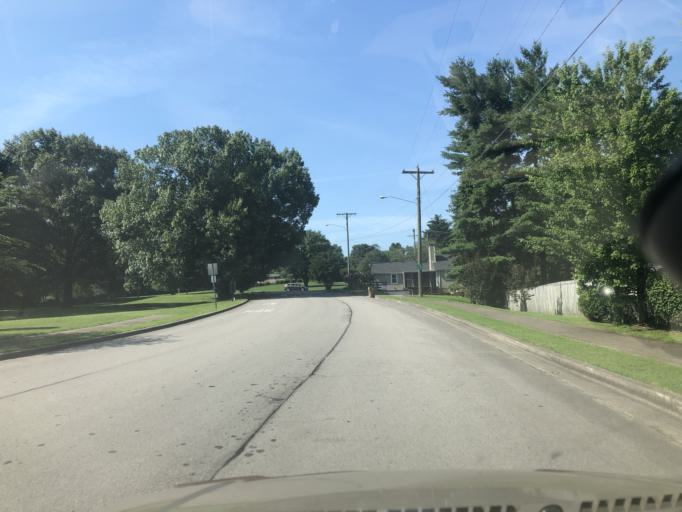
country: US
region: Tennessee
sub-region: Davidson County
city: Lakewood
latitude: 36.2330
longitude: -86.6956
